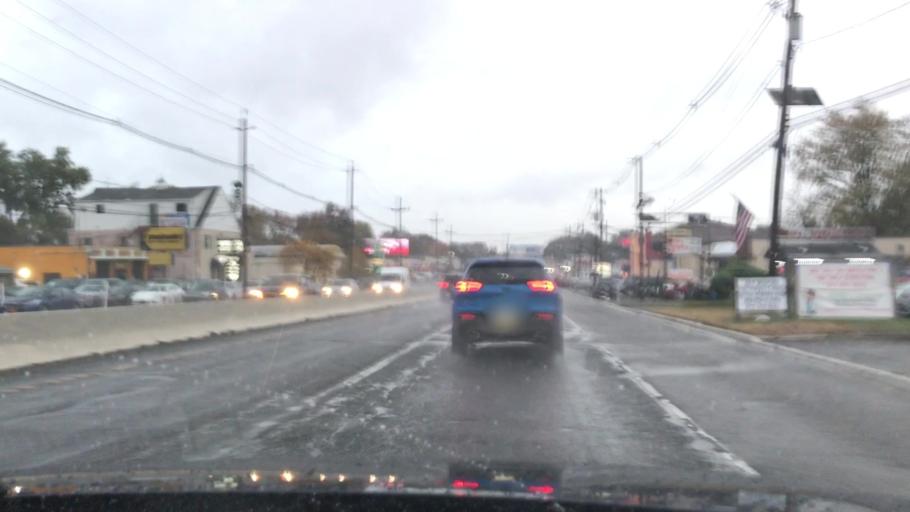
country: US
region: New Jersey
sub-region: Bergen County
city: Lodi
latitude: 40.8764
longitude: -74.0727
